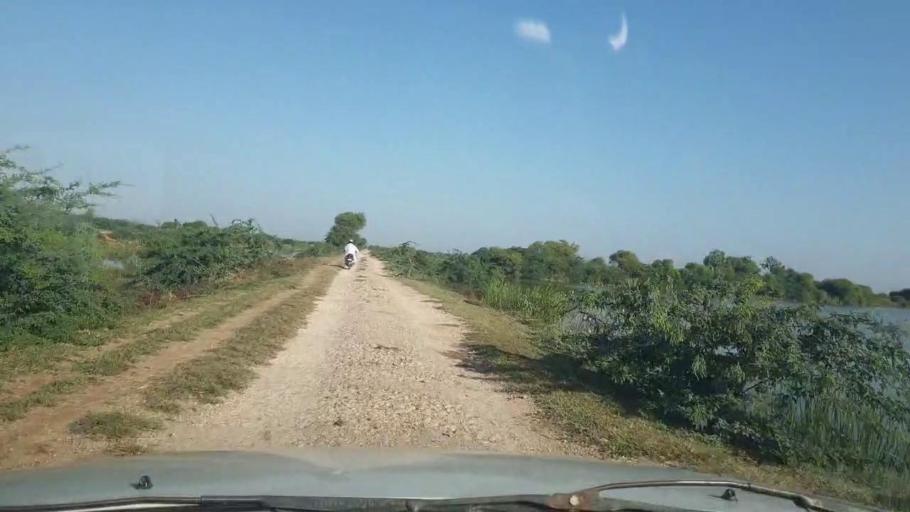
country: PK
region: Sindh
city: Chuhar Jamali
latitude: 24.5442
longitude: 67.9118
